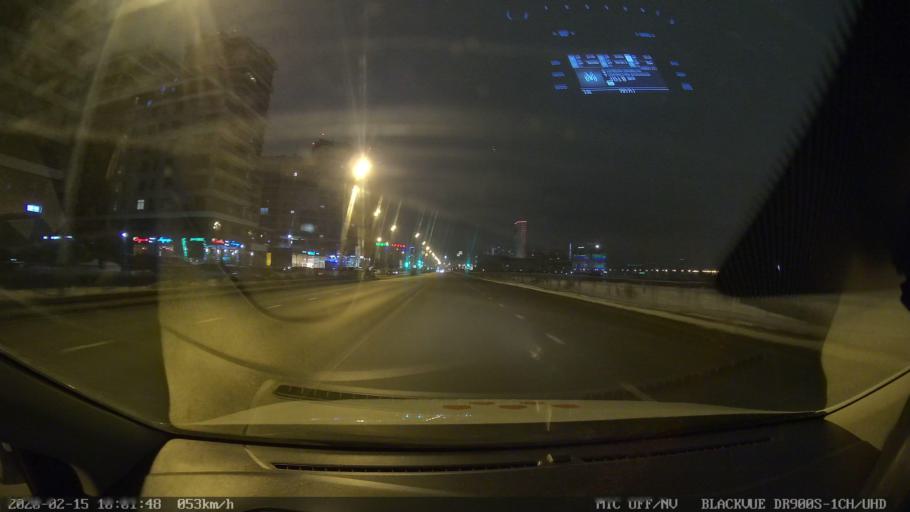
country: RU
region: Tatarstan
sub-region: Gorod Kazan'
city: Kazan
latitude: 55.8160
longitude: 49.1190
